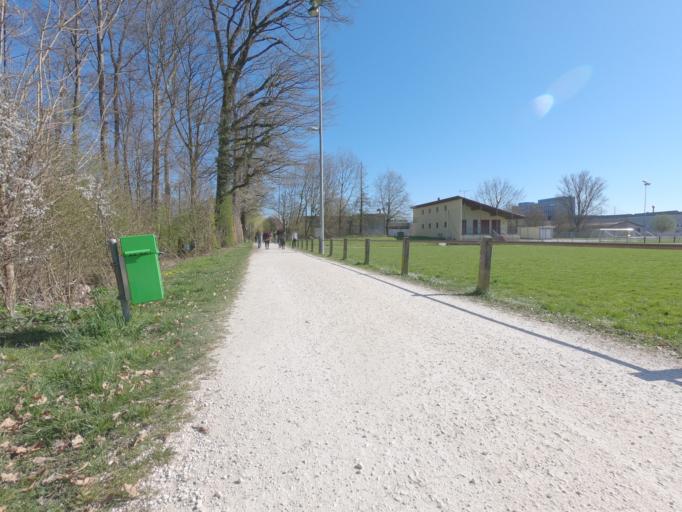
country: CH
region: Solothurn
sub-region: Bezirk Wasseramt
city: Zuchwil
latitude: 47.2129
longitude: 7.5558
